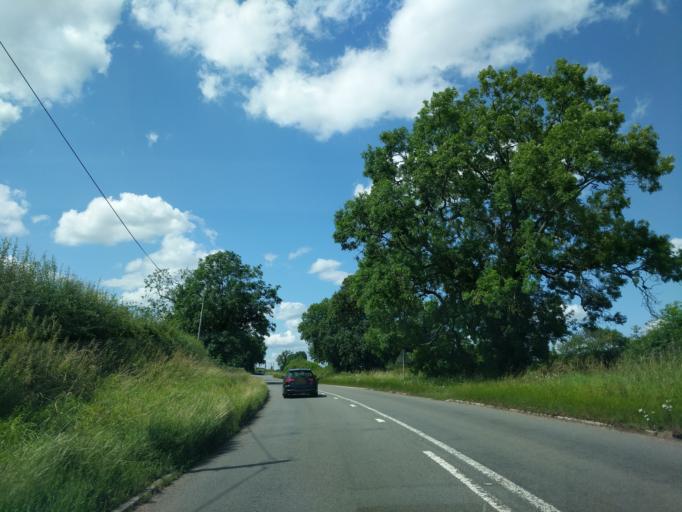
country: GB
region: England
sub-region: Staffordshire
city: Uttoxeter
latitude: 52.9299
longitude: -1.9220
